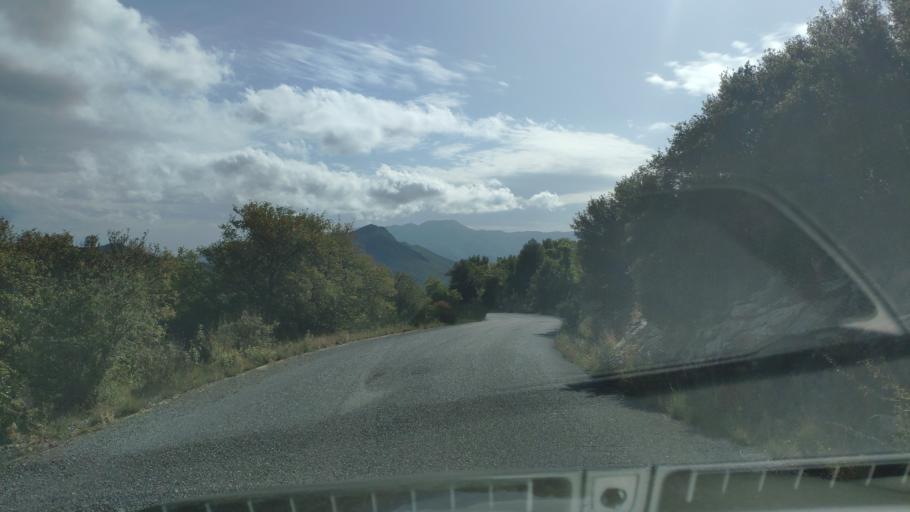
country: GR
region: Peloponnese
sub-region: Nomos Arkadias
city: Dimitsana
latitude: 37.5657
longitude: 22.0072
